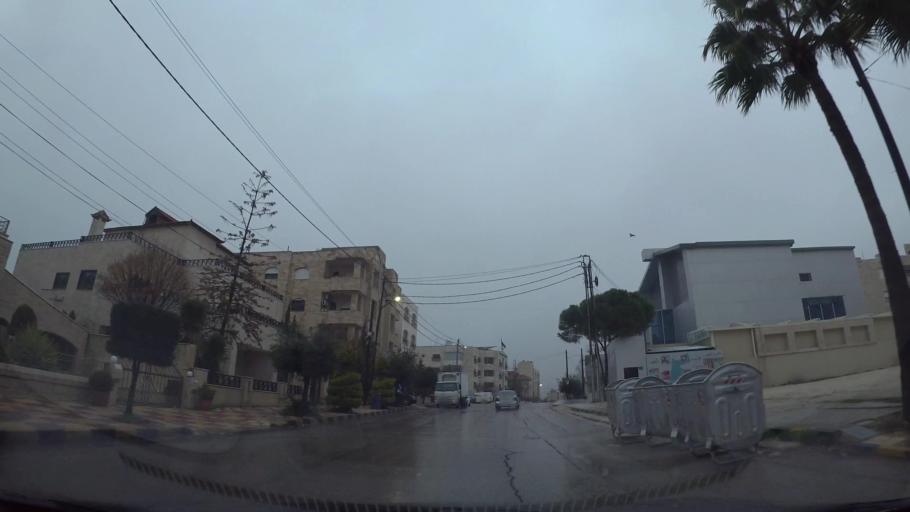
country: JO
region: Amman
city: Wadi as Sir
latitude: 31.9713
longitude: 35.8709
